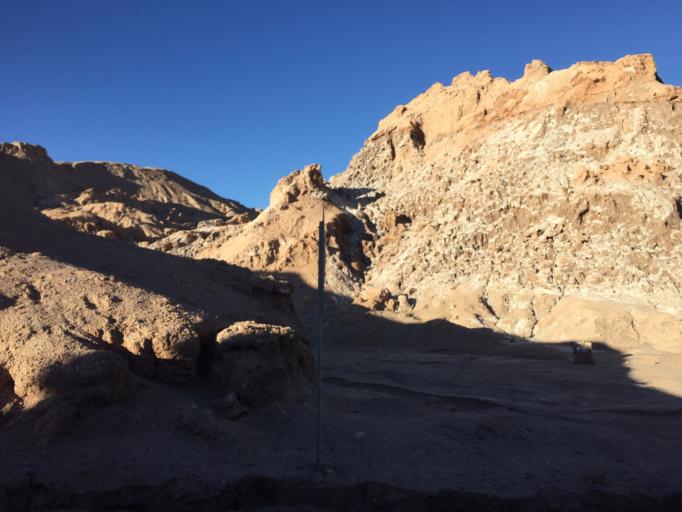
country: CL
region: Antofagasta
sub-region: Provincia de El Loa
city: San Pedro de Atacama
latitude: -22.9456
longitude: -68.2770
